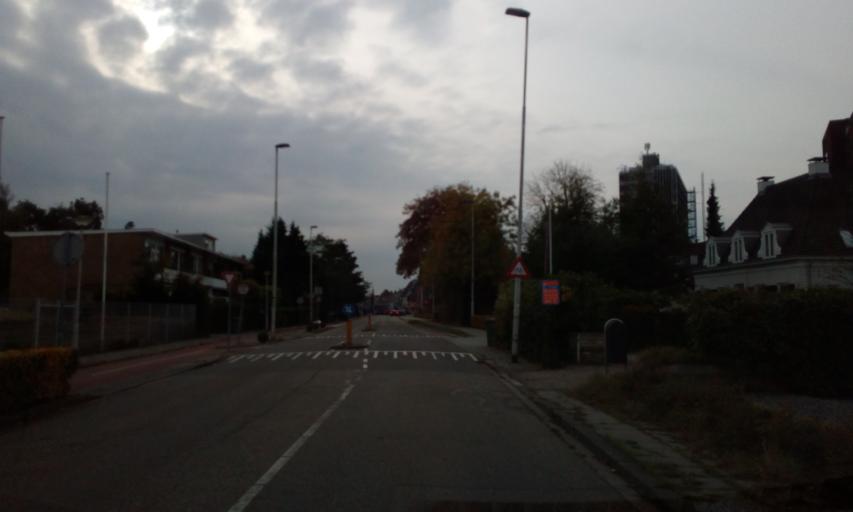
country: NL
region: South Holland
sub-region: Gemeente Lansingerland
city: Bergschenhoek
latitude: 51.9607
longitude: 4.4952
